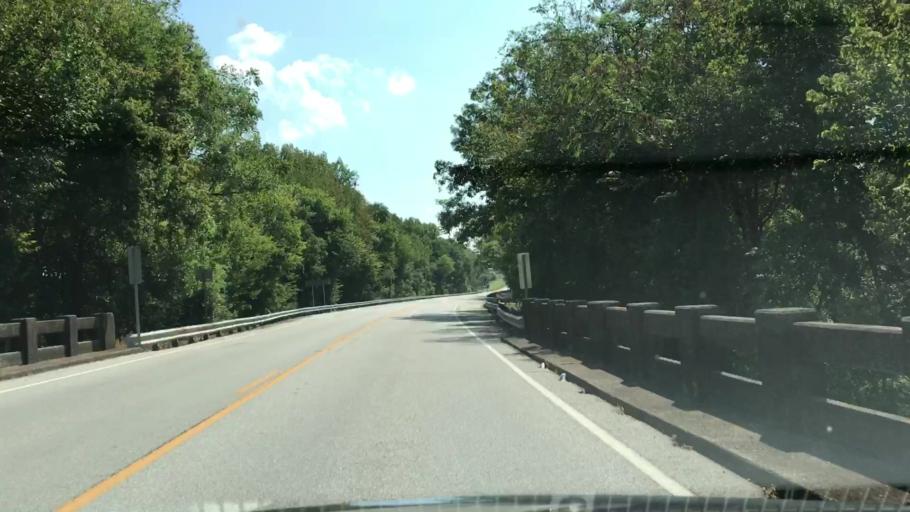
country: US
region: Tennessee
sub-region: Trousdale County
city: Hartsville
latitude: 36.3612
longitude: -86.0560
